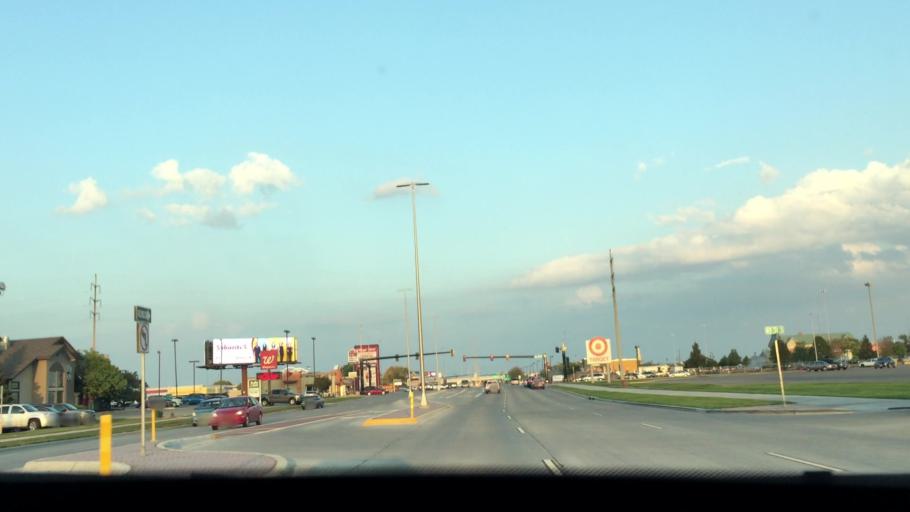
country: US
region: North Dakota
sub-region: Cass County
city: West Fargo
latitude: 46.8618
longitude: -96.8535
